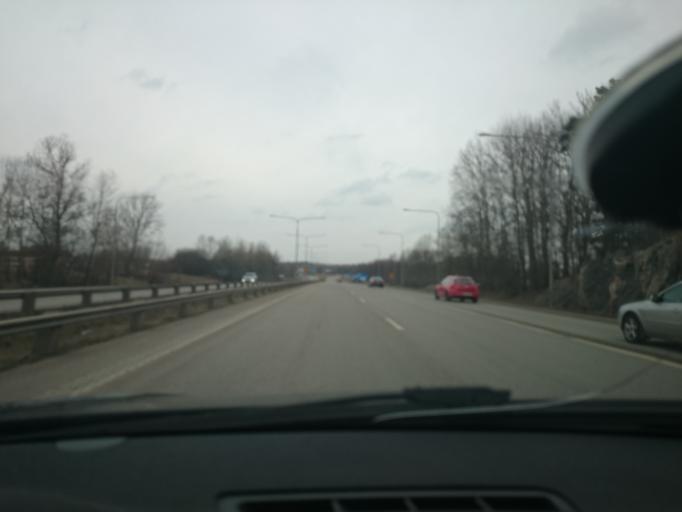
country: SE
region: OEstergoetland
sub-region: Norrkopings Kommun
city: Norrkoping
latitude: 58.5758
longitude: 16.2131
